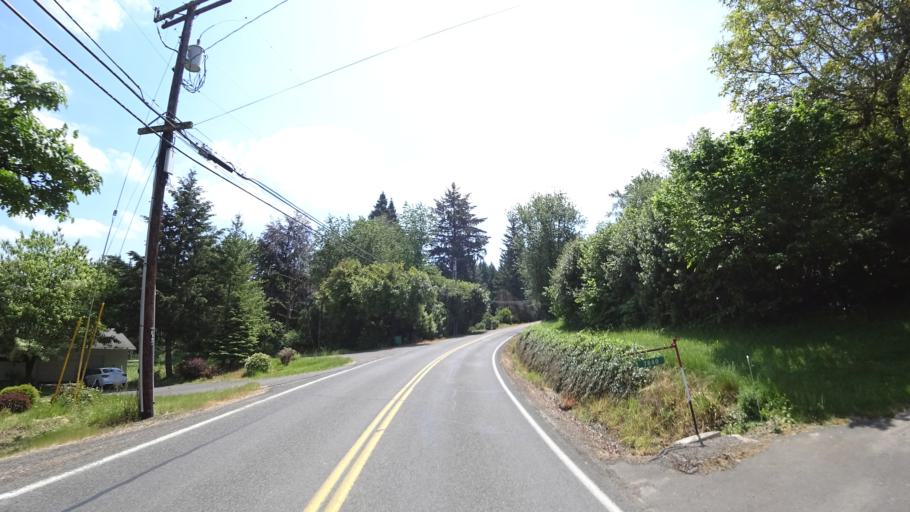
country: US
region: Oregon
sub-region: Clackamas County
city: Happy Valley
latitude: 45.4662
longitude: -122.5048
